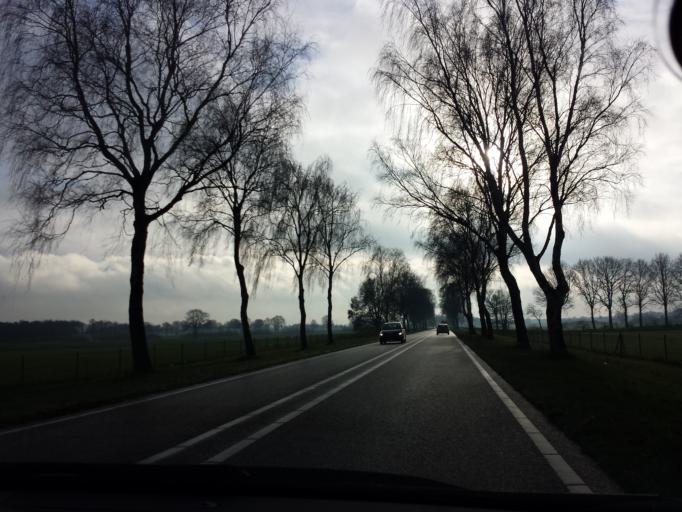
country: NL
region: North Brabant
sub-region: Gemeente Landerd
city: Zeeland
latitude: 51.7181
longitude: 5.6688
